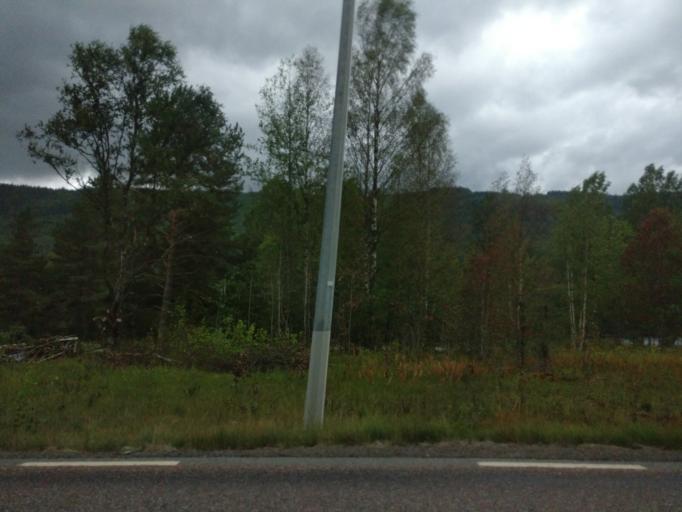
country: SE
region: Vaermland
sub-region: Torsby Kommun
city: Torsby
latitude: 60.7138
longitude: 12.8822
